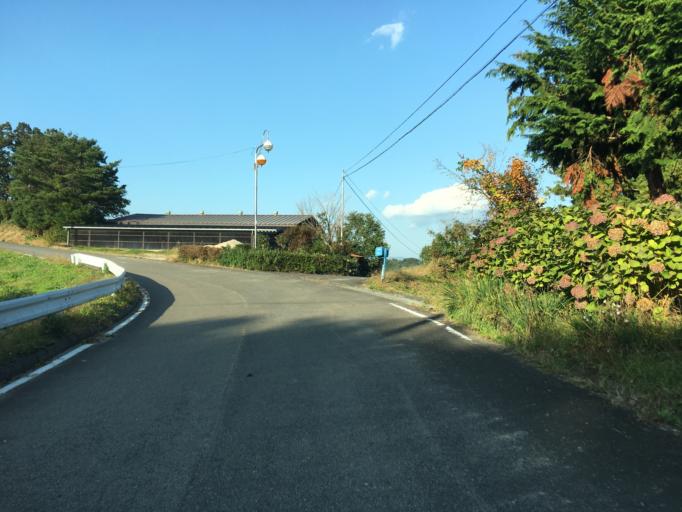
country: JP
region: Fukushima
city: Nihommatsu
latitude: 37.6349
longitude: 140.5648
